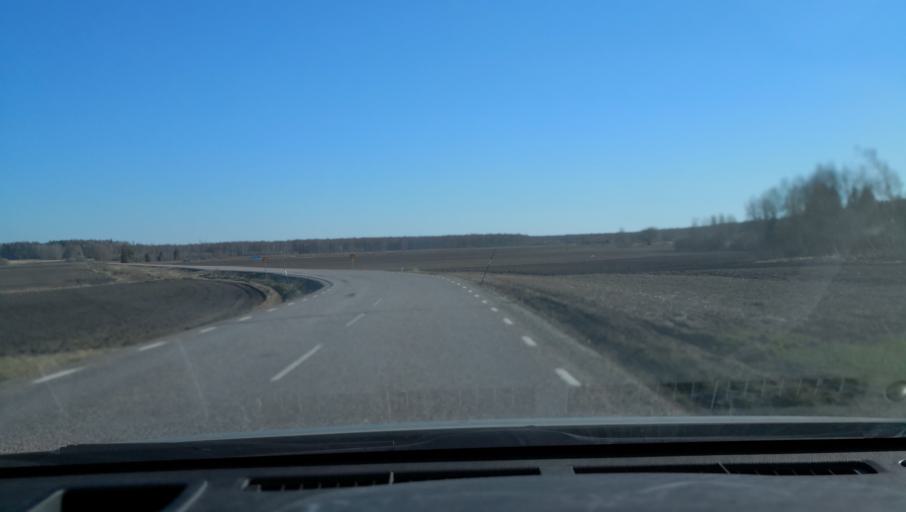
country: SE
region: Vaestmanland
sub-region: Vasteras
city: Skultuna
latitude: 59.9038
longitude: 16.3488
